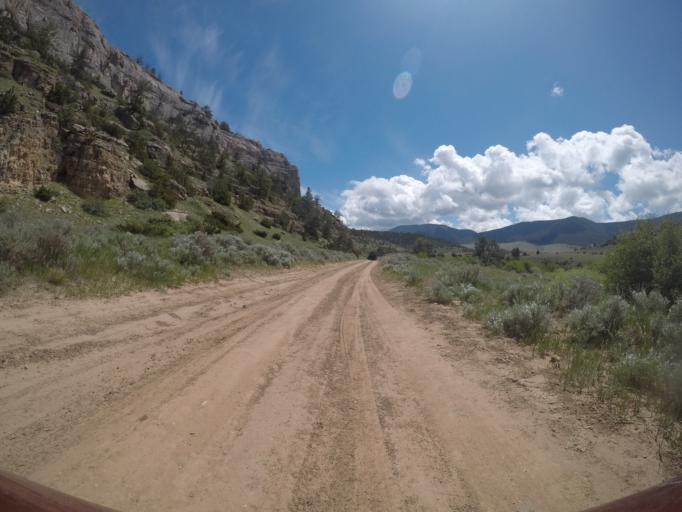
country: US
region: Wyoming
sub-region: Big Horn County
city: Lovell
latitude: 45.2241
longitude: -108.5962
